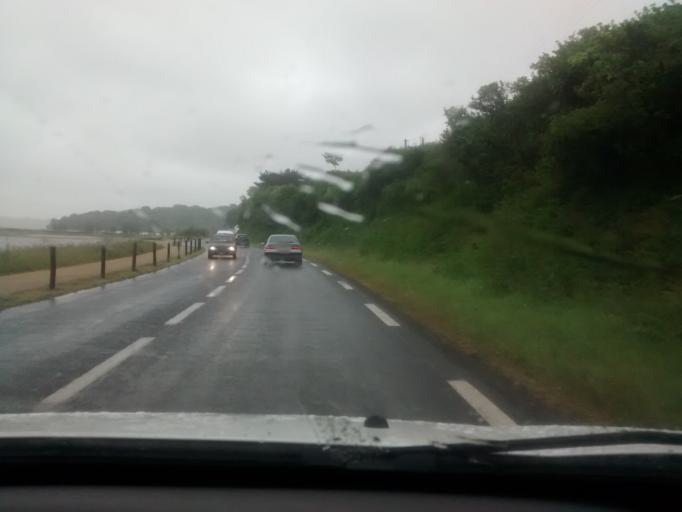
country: FR
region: Brittany
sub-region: Departement des Cotes-d'Armor
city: Perros-Guirec
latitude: 48.7973
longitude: -3.4347
